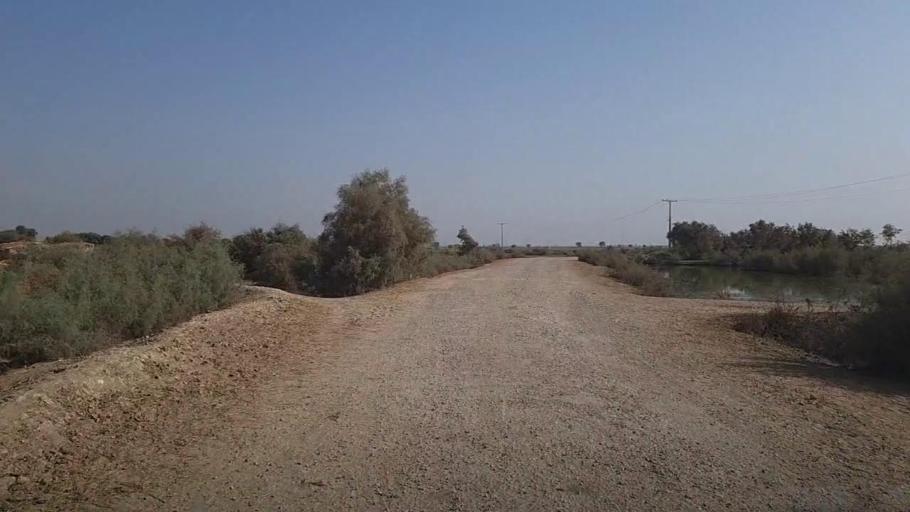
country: PK
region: Sindh
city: Kandhkot
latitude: 28.3810
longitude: 69.3354
